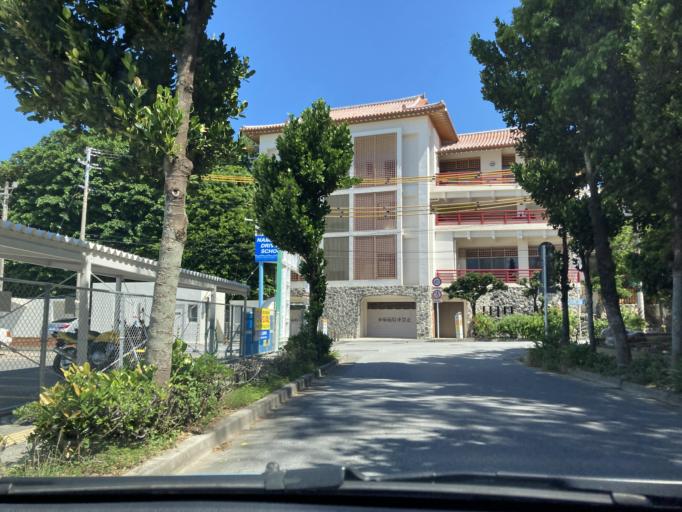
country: JP
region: Okinawa
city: Naha-shi
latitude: 26.2199
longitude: 127.6707
